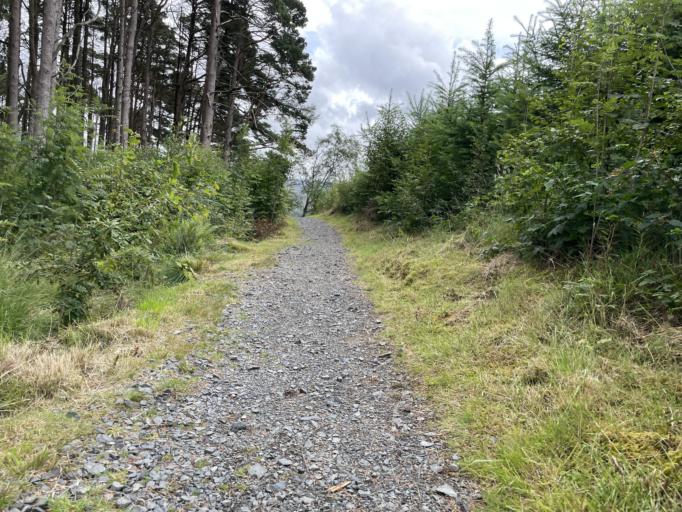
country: GB
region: Scotland
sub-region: Dumfries and Galloway
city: Newton Stewart
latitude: 55.0872
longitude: -4.4940
